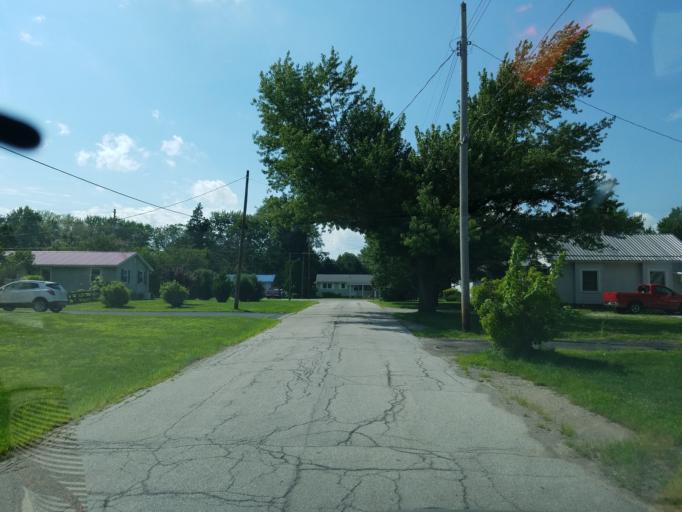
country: US
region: Ohio
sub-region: Ashland County
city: Ashland
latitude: 40.8773
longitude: -82.3282
